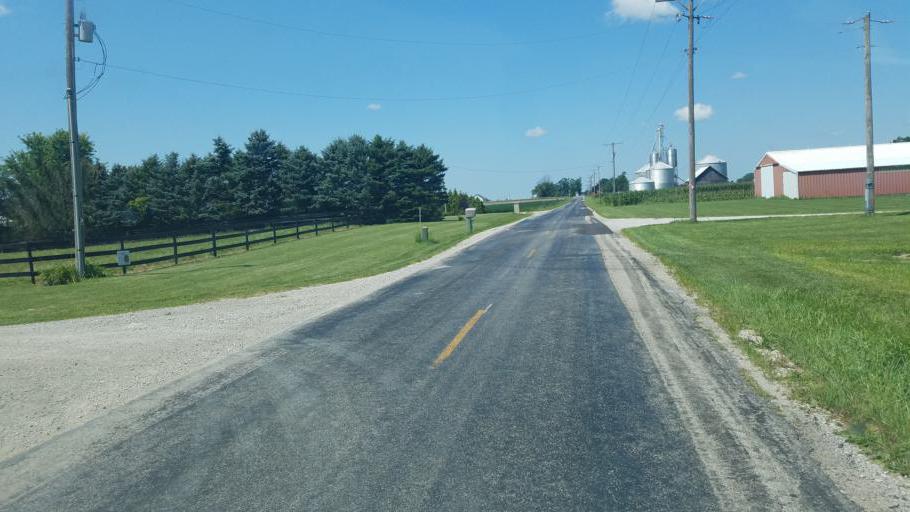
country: US
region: Ohio
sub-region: Marion County
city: Prospect
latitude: 40.4839
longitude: -83.0960
